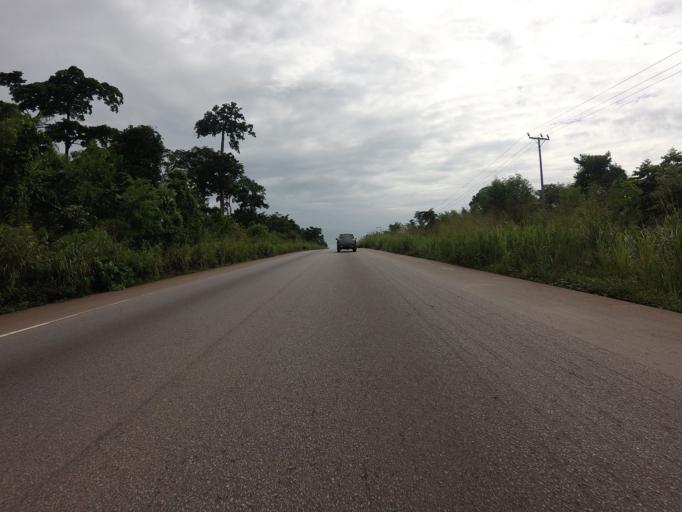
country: GH
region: Eastern
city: Nkawkaw
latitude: 6.6018
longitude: -0.8719
